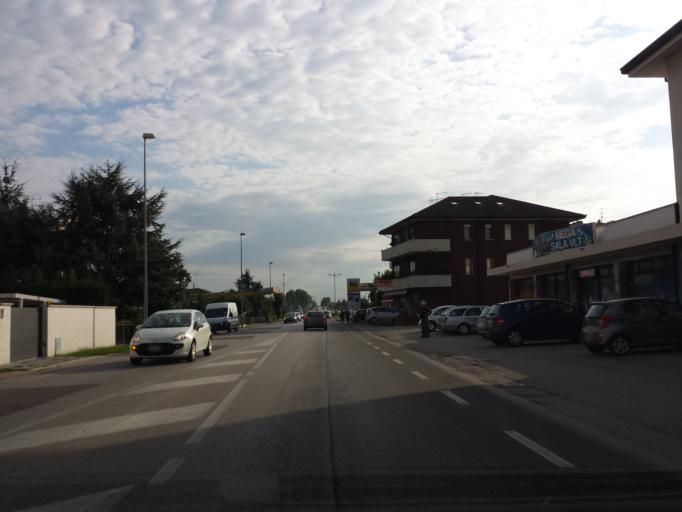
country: IT
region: Veneto
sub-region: Provincia di Rovigo
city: Rovigo
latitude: 45.0601
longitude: 11.7922
